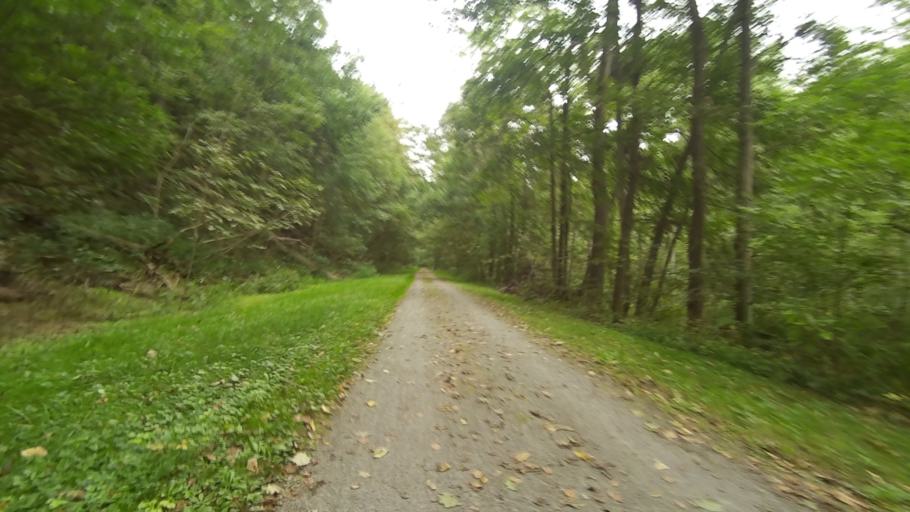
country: US
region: Pennsylvania
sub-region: Blair County
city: Williamsburg
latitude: 40.5588
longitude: -78.1406
